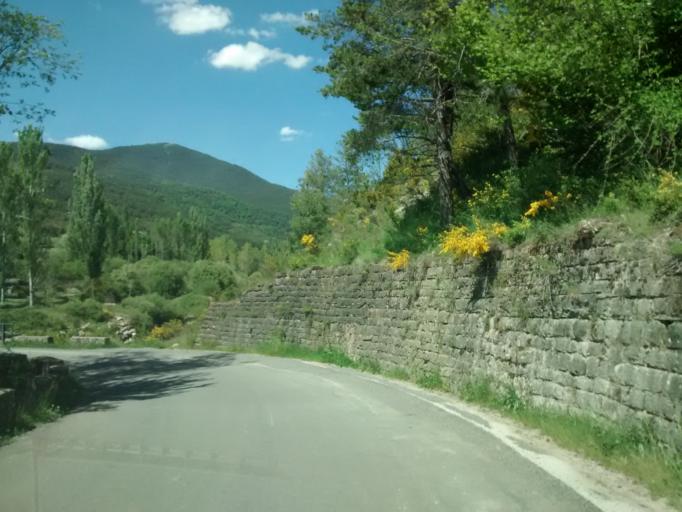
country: ES
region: Aragon
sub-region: Provincia de Huesca
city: Borau
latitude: 42.6875
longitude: -0.6208
